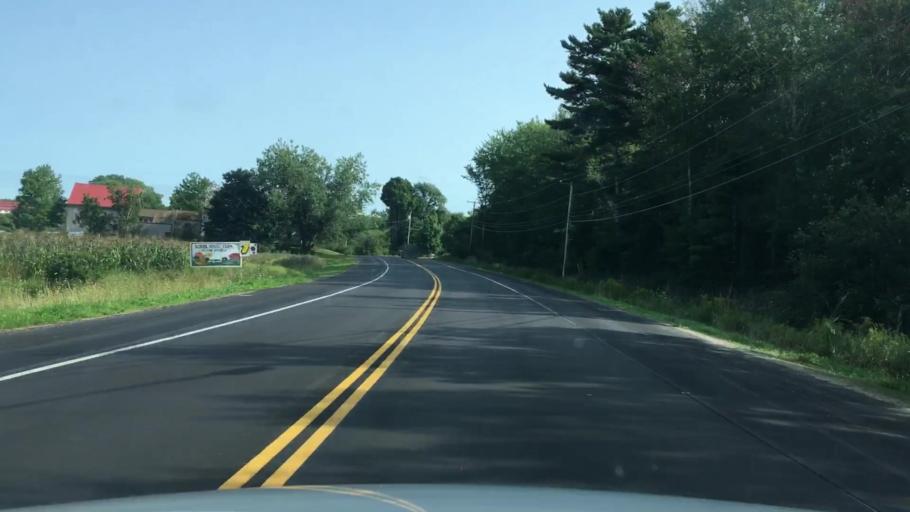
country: US
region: Maine
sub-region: Knox County
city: Warren
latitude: 44.1016
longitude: -69.2491
